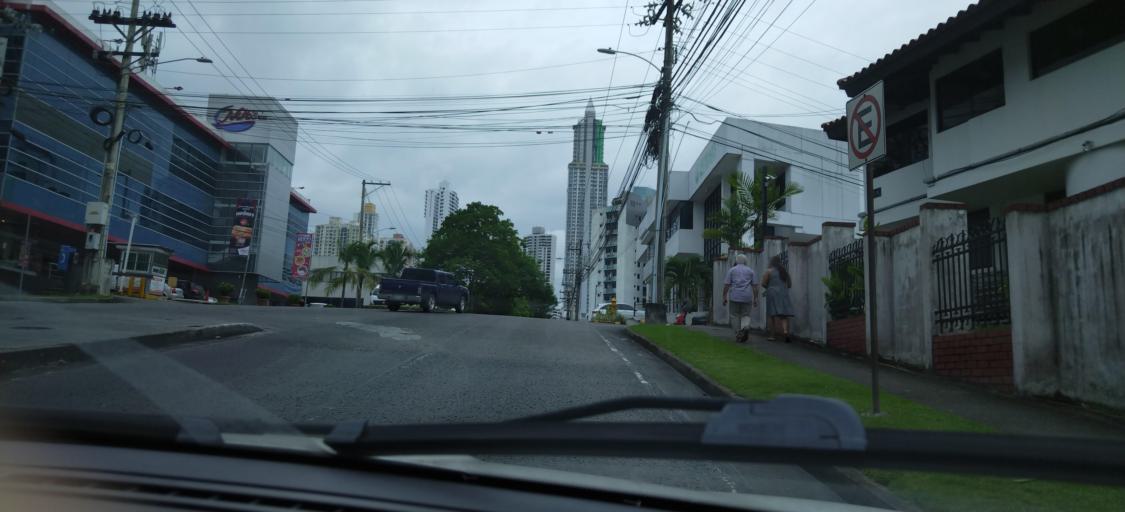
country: PA
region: Panama
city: Panama
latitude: 9.0098
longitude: -79.5370
